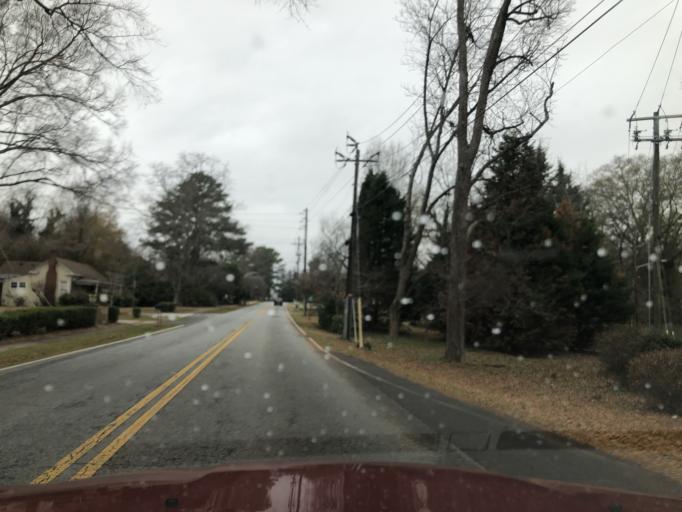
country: US
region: Georgia
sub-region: Clayton County
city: Jonesboro
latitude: 33.5303
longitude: -84.3569
